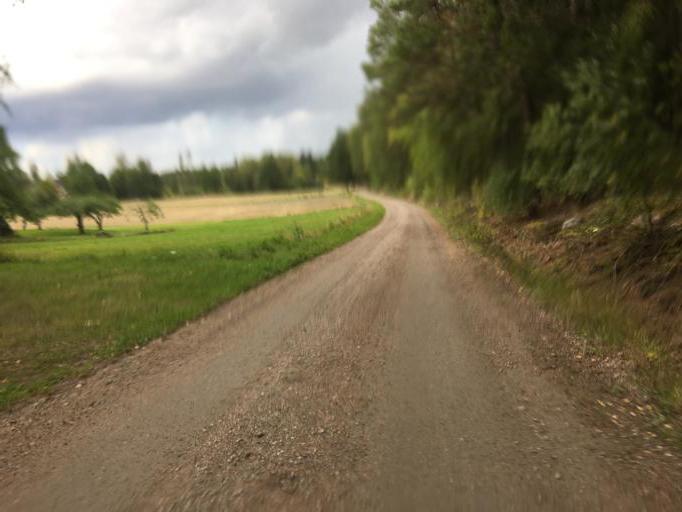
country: SE
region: Soedermanland
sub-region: Eskilstuna Kommun
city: Arla
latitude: 59.4576
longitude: 16.6791
